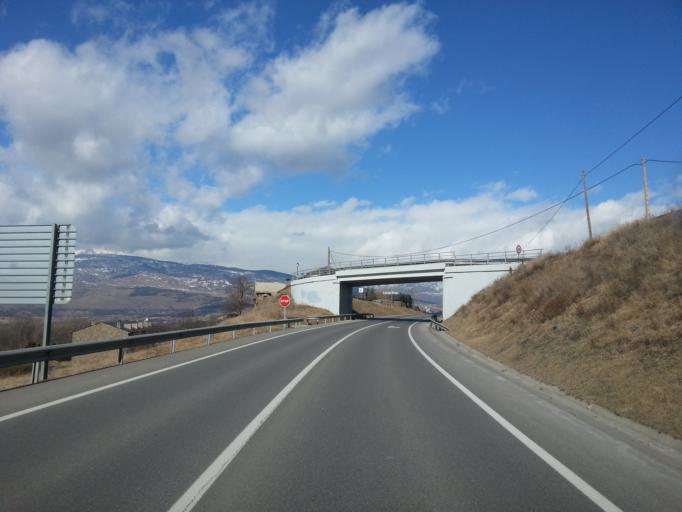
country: ES
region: Catalonia
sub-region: Provincia de Girona
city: Alp
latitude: 42.3827
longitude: 1.8921
